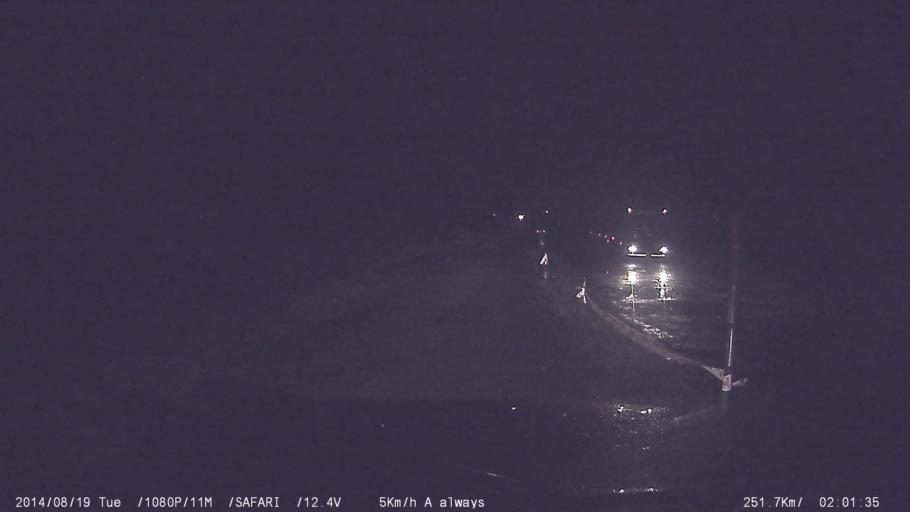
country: IN
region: Tamil Nadu
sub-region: Coimbatore
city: Madukkarai
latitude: 10.8716
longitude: 76.8890
